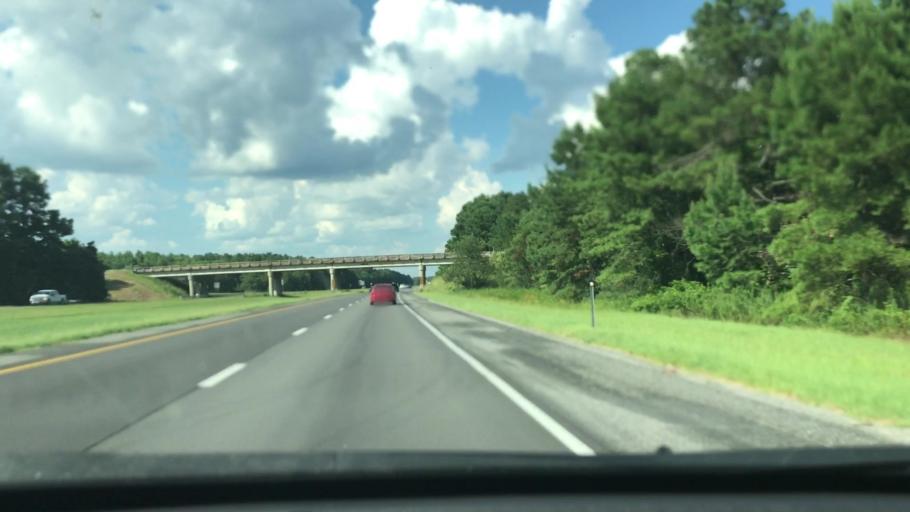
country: US
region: South Carolina
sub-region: Clarendon County
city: Manning
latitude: 33.8589
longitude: -80.1138
